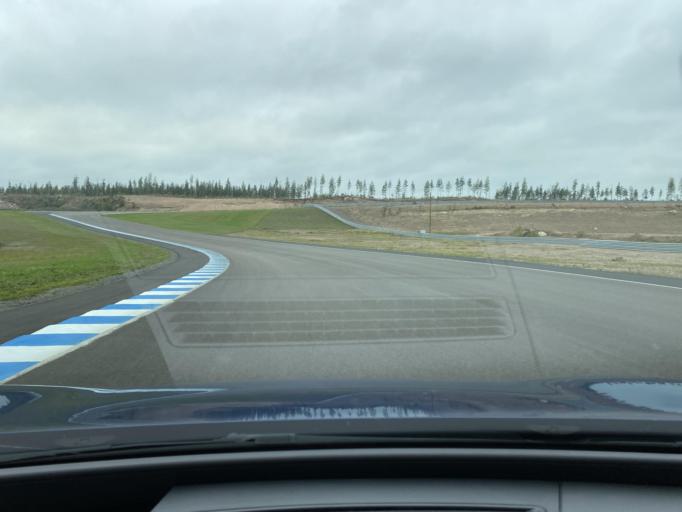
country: FI
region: Kymenlaakso
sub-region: Kouvola
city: Iitti
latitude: 60.8785
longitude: 26.4869
